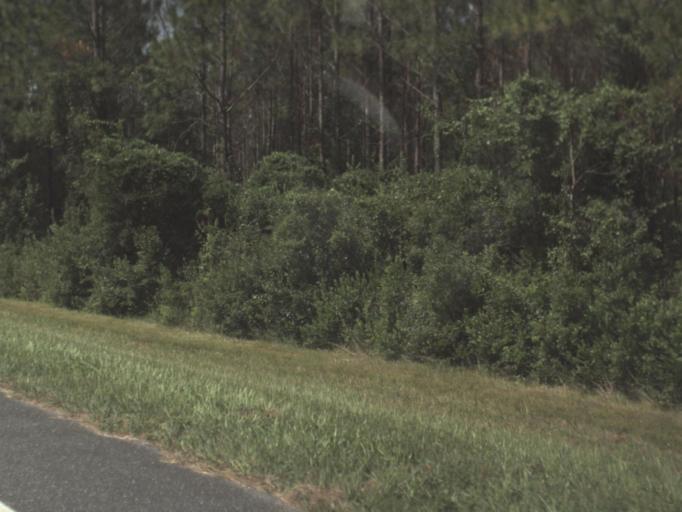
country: US
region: Florida
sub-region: Baker County
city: Macclenny
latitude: 30.3197
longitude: -82.1250
